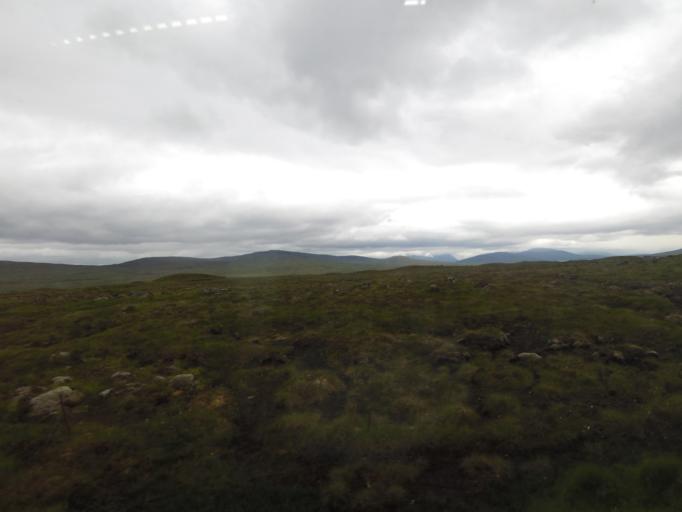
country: GB
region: Scotland
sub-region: Highland
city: Spean Bridge
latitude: 56.7241
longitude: -4.6339
